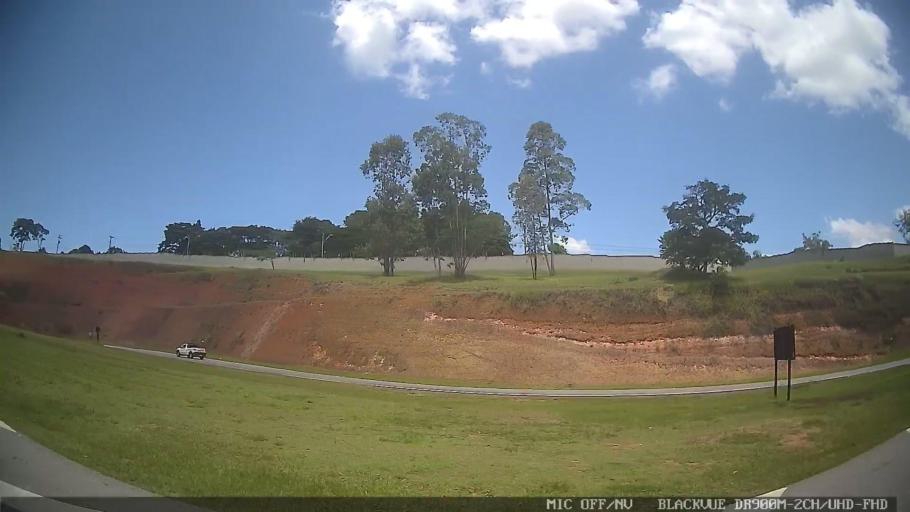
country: BR
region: Sao Paulo
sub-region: Santa Branca
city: Santa Branca
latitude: -23.3181
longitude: -45.7270
